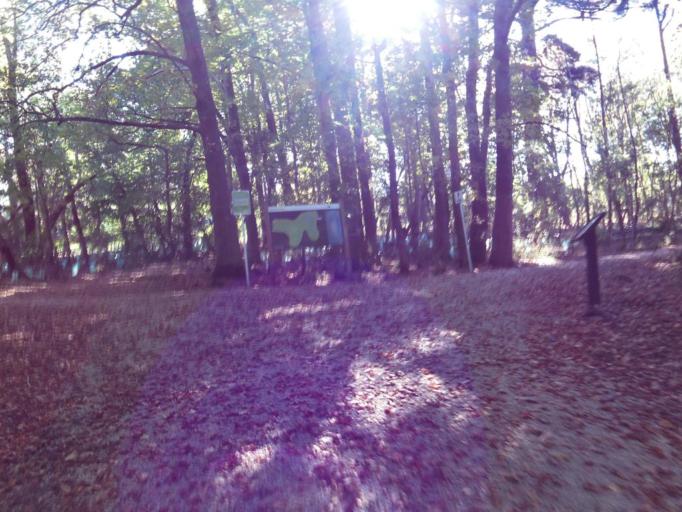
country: AU
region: Victoria
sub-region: Cardinia
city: Emerald
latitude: -37.9301
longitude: 145.4500
